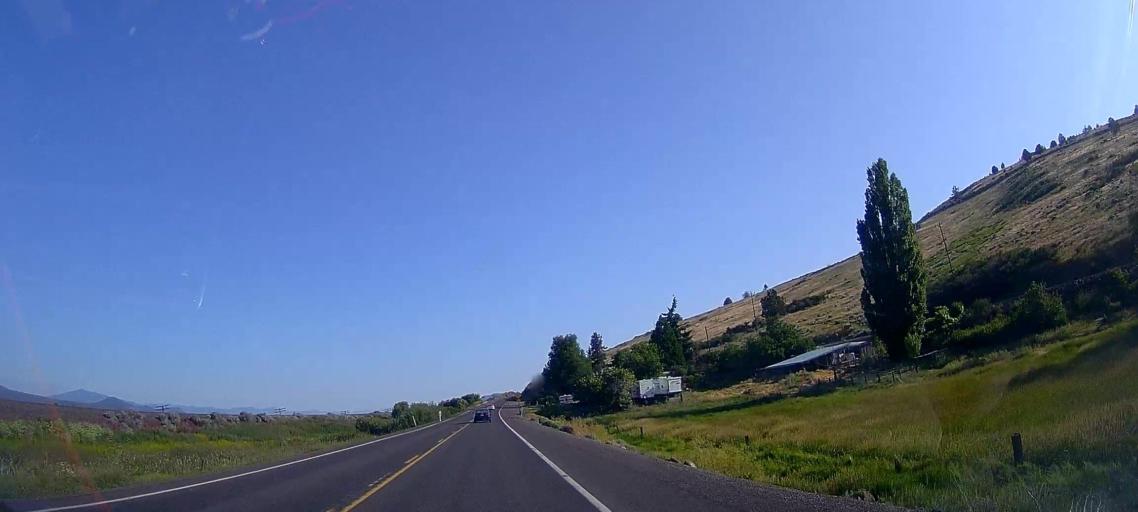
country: US
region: Oregon
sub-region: Klamath County
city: Klamath Falls
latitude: 42.2924
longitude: -121.8154
